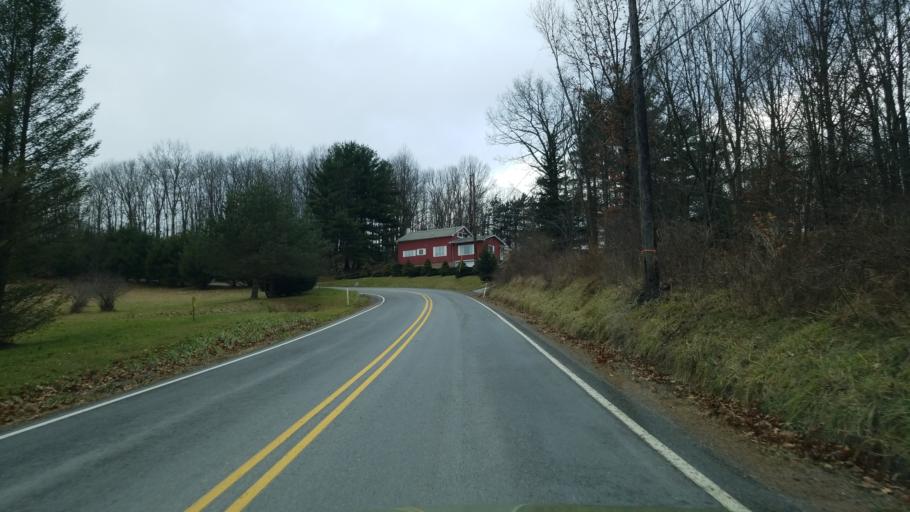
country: US
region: Pennsylvania
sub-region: Clearfield County
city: Hyde
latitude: 41.0347
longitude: -78.4802
